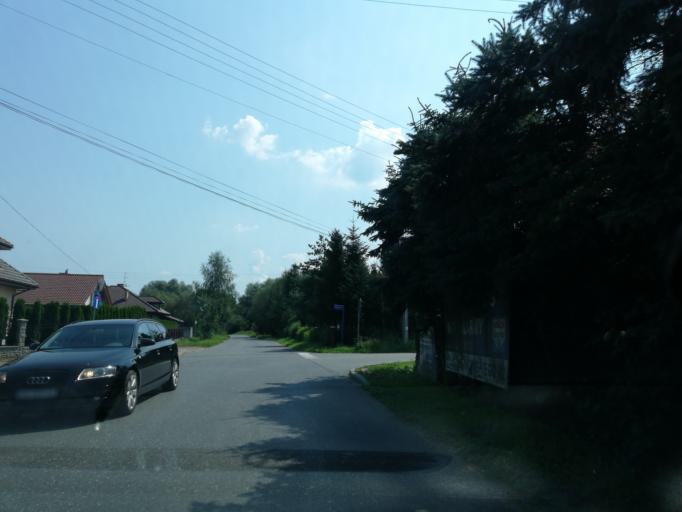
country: PL
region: Lesser Poland Voivodeship
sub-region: Powiat nowosadecki
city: Chelmiec
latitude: 49.6435
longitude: 20.6754
